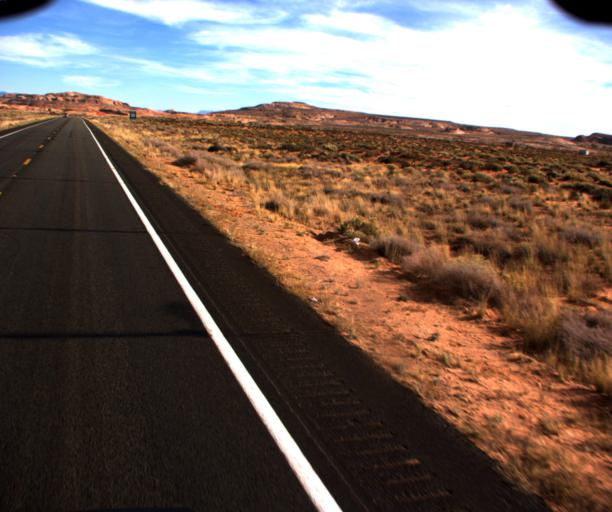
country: US
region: Arizona
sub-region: Apache County
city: Many Farms
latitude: 36.9298
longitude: -109.6231
